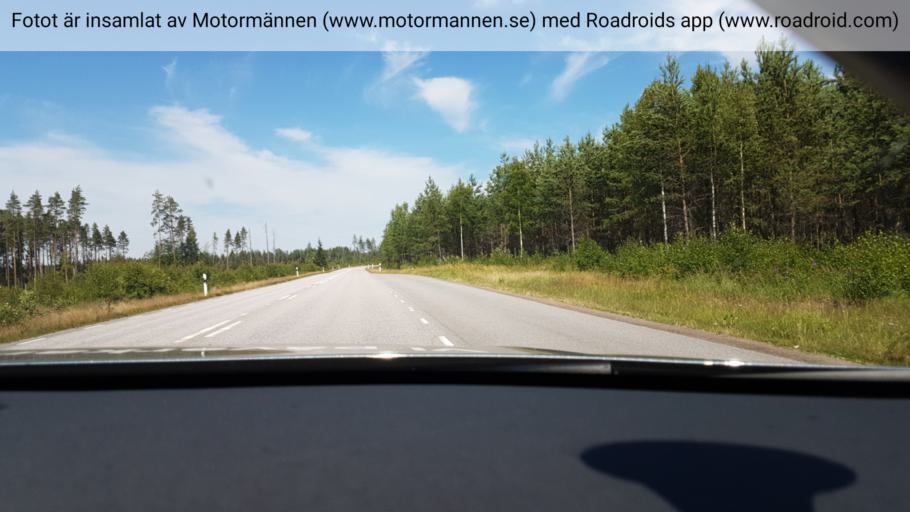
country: SE
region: Vaestra Goetaland
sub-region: Skovde Kommun
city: Stopen
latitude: 58.4403
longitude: 13.9353
